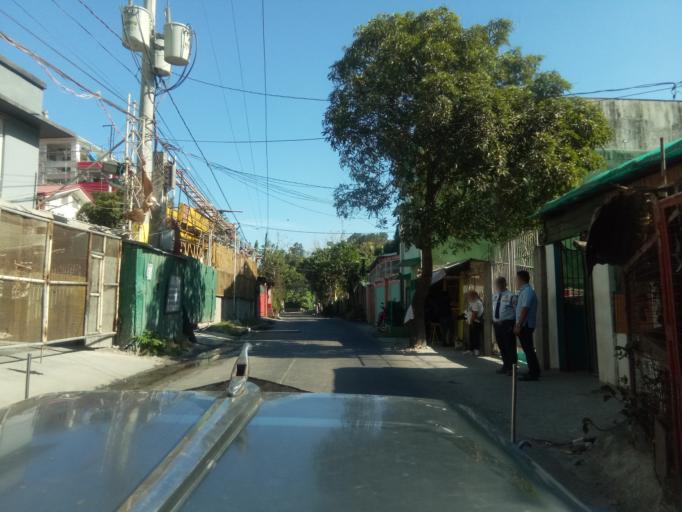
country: PH
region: Calabarzon
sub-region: Province of Cavite
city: Dasmarinas
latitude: 14.3261
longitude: 120.9453
